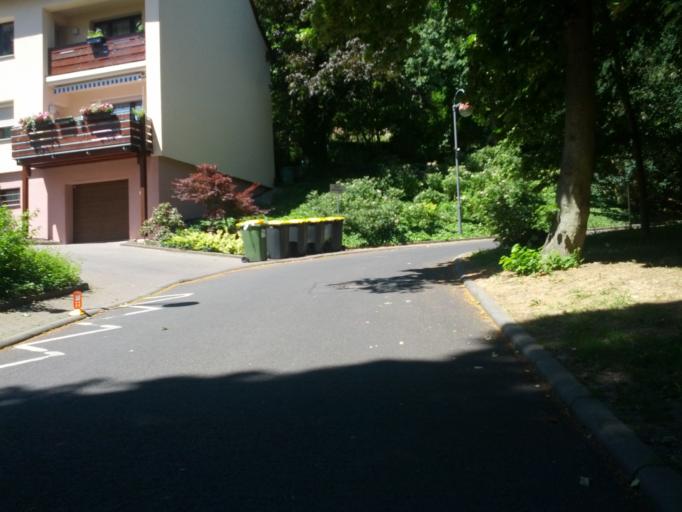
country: DE
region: Thuringia
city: Eisenach
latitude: 50.9694
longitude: 10.3180
